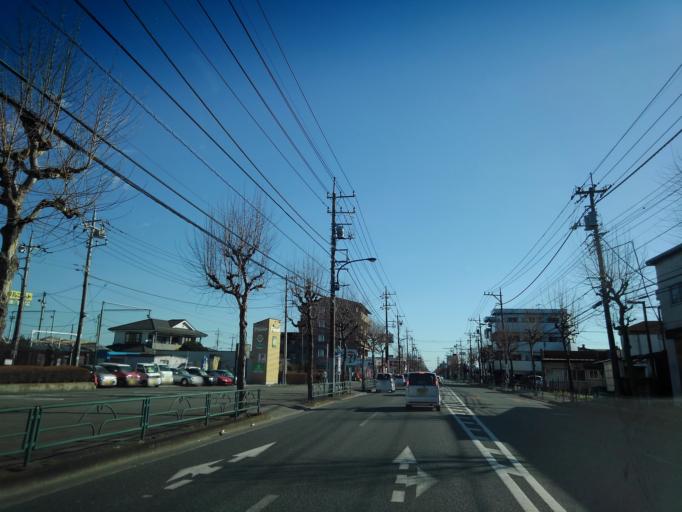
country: JP
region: Tokyo
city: Fussa
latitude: 35.7645
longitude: 139.3554
